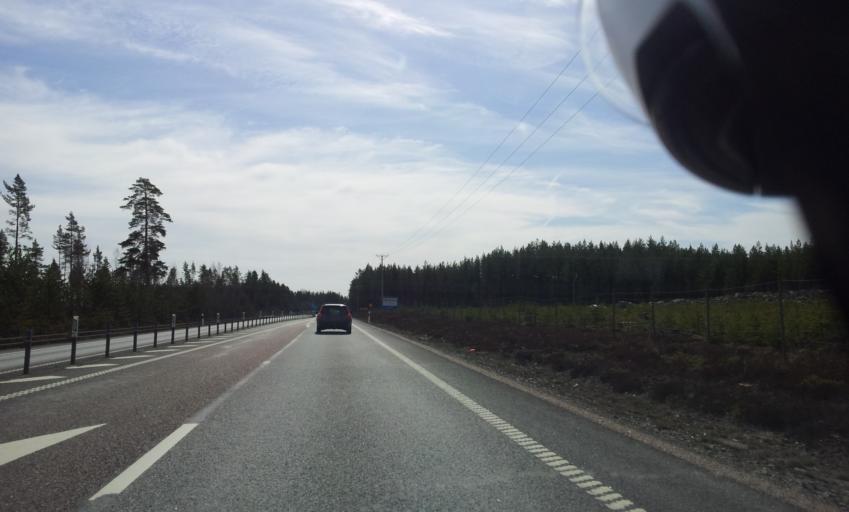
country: SE
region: Gaevleborg
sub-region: Gavle Kommun
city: Norrsundet
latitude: 61.0369
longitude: 16.9682
